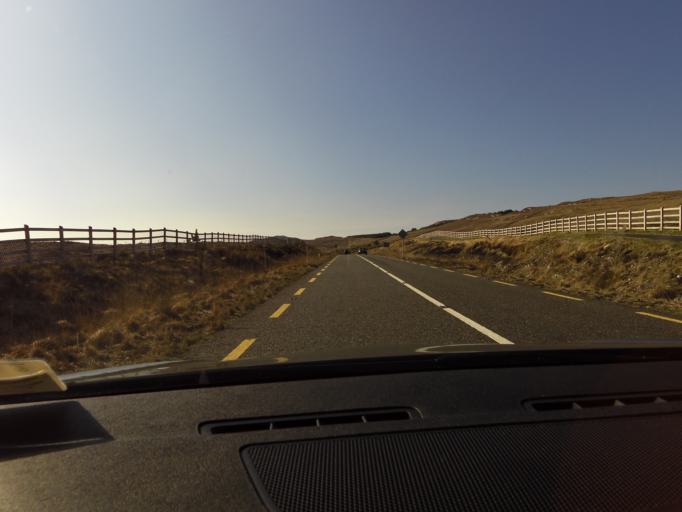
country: IE
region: Connaught
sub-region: County Galway
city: Clifden
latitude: 53.4785
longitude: -9.9133
